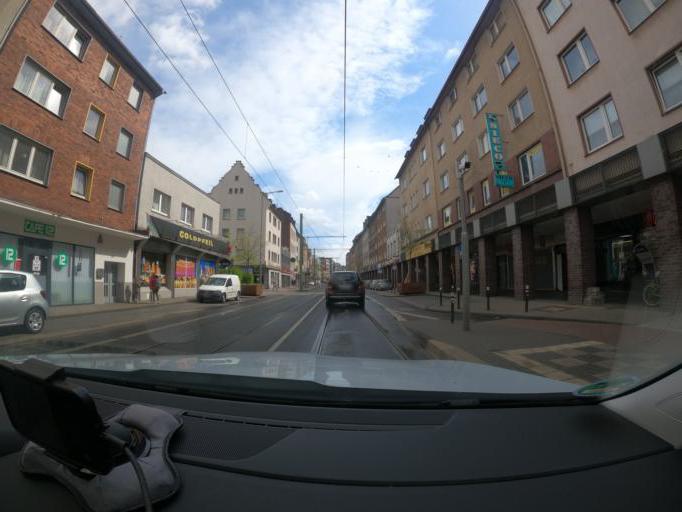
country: DE
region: North Rhine-Westphalia
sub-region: Regierungsbezirk Dusseldorf
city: Hochfeld
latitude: 51.4214
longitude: 6.7543
